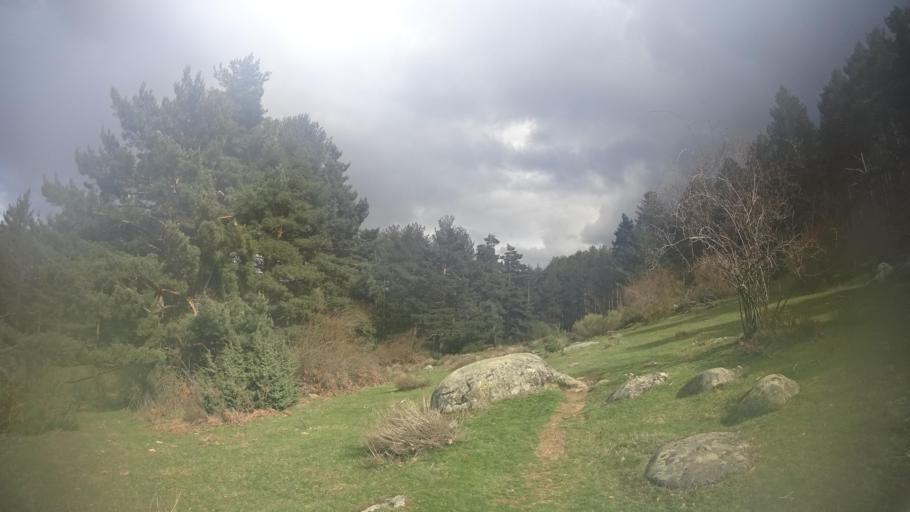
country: ES
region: Madrid
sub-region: Provincia de Madrid
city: Canencia
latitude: 40.8748
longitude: -3.7705
